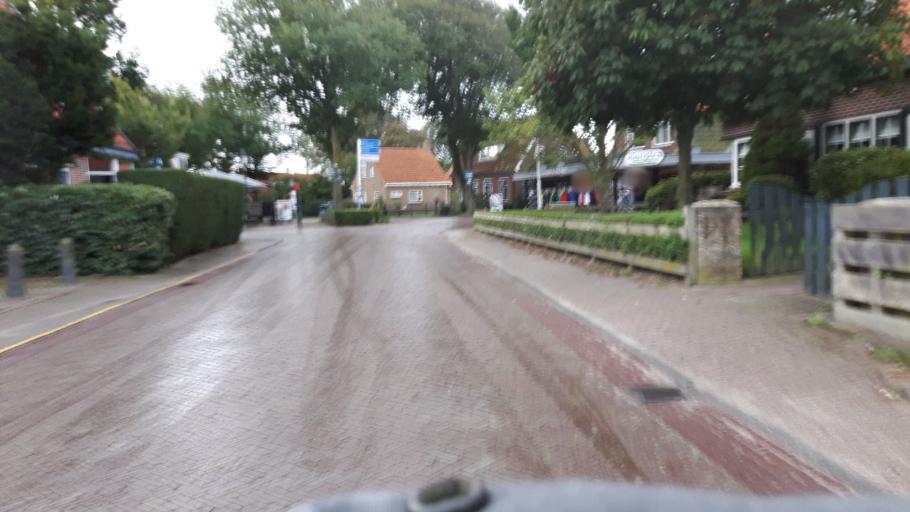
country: NL
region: Friesland
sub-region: Gemeente Ameland
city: Nes
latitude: 53.4468
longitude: 5.7696
